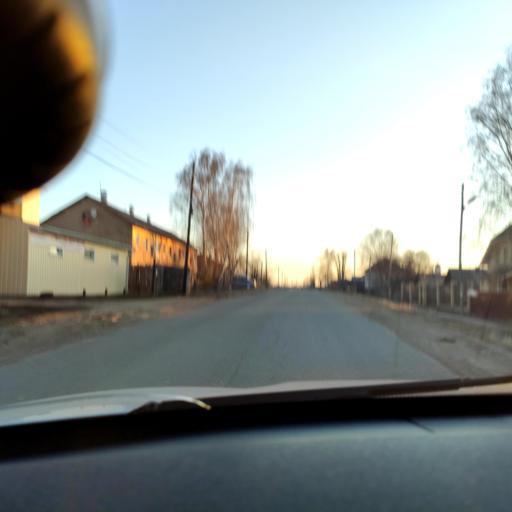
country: RU
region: Perm
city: Kultayevo
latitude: 57.9307
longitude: 55.8766
